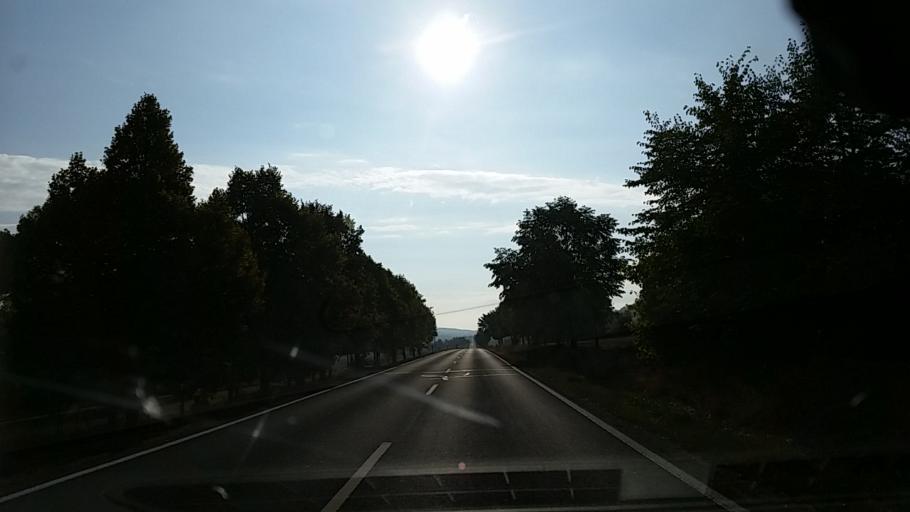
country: DE
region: Thuringia
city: Kleinfurra
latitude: 51.3924
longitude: 10.8030
